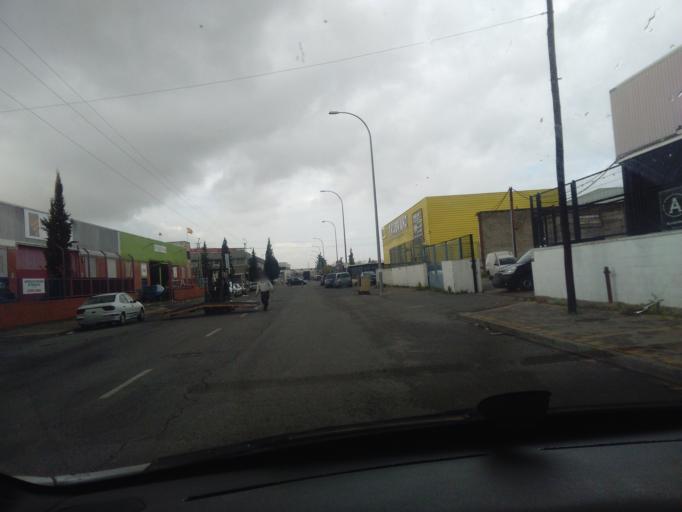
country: ES
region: Andalusia
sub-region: Provincia de Sevilla
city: Sevilla
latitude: 37.3770
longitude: -5.9248
